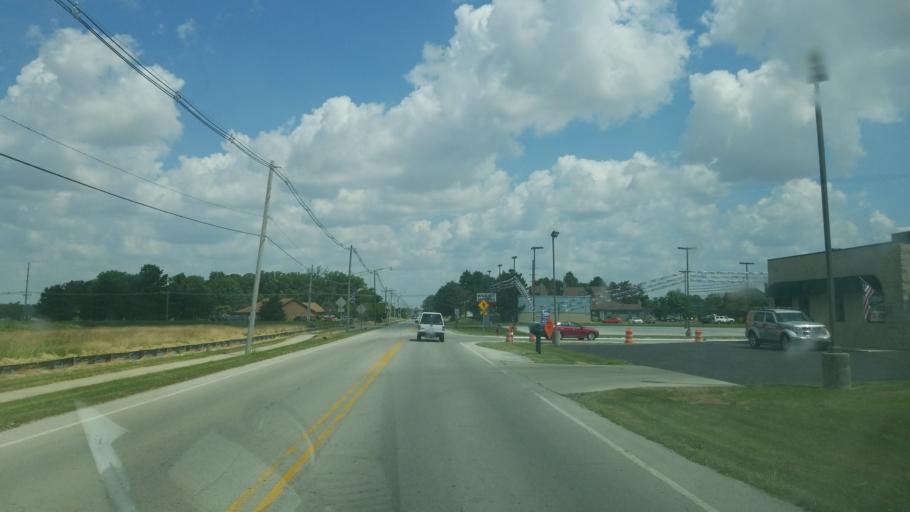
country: US
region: Ohio
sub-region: Auglaize County
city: Wapakoneta
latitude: 40.5824
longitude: -84.2028
